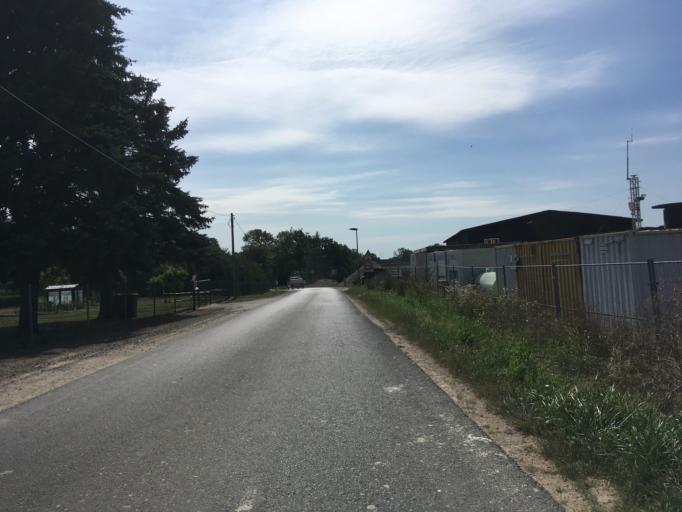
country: DE
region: Brandenburg
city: Gramzow
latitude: 53.2796
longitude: 14.0652
